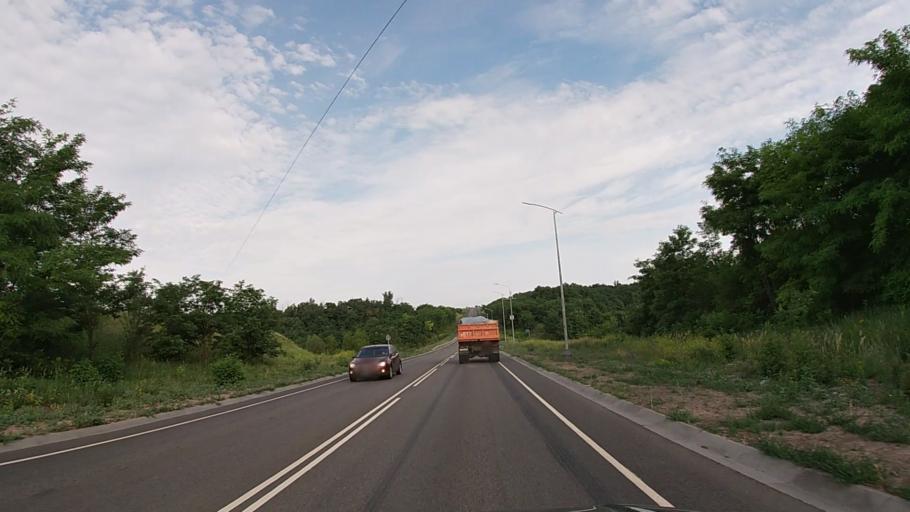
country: RU
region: Belgorod
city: Severnyy
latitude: 50.6677
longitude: 36.4922
